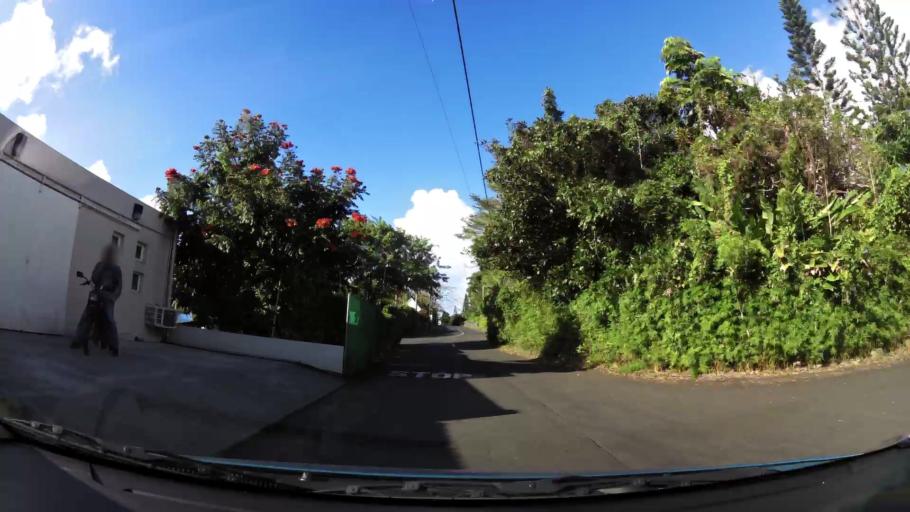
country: MU
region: Plaines Wilhems
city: Curepipe
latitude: -20.3130
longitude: 57.5045
